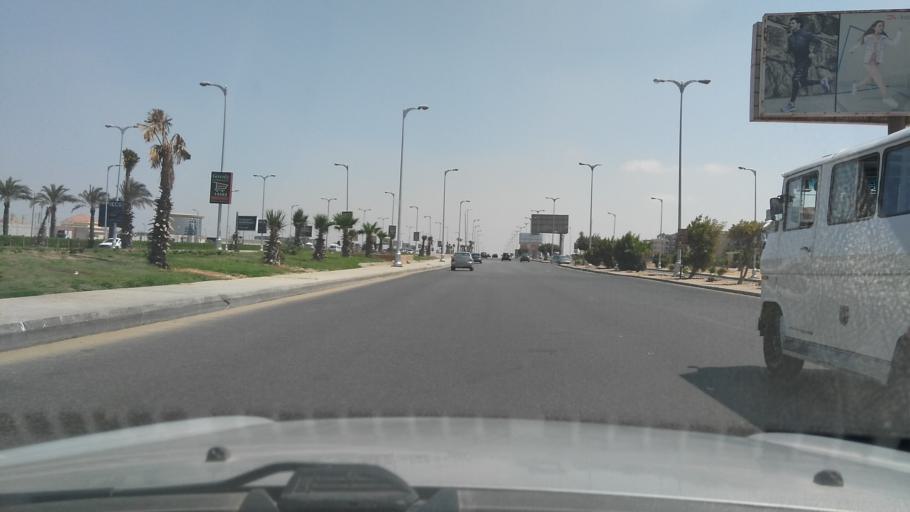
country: EG
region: Al Jizah
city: Madinat Sittah Uktubar
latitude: 30.0031
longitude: 30.9732
